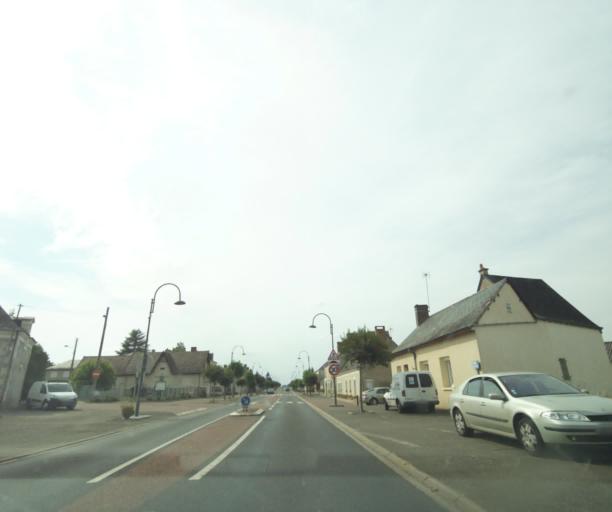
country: FR
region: Centre
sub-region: Departement d'Indre-et-Loire
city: Saint-Christophe-sur-le-Nais
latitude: 47.6649
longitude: 0.4718
